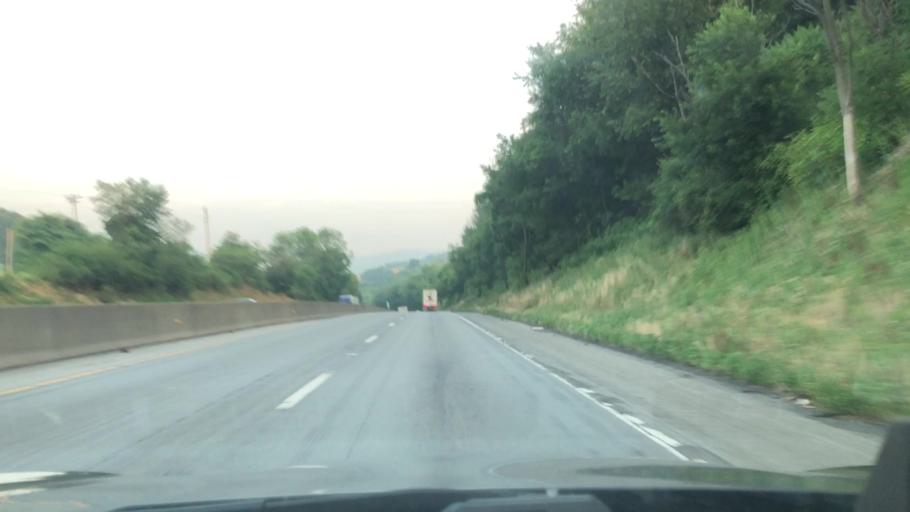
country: US
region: Pennsylvania
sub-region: Berks County
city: Kutztown
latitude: 40.5792
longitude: -75.8202
